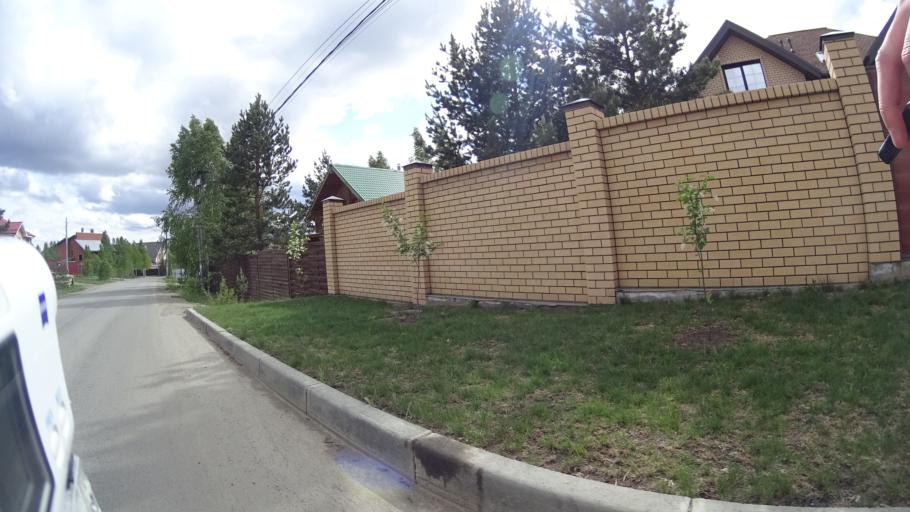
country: RU
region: Chelyabinsk
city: Sargazy
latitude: 55.1594
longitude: 61.2430
